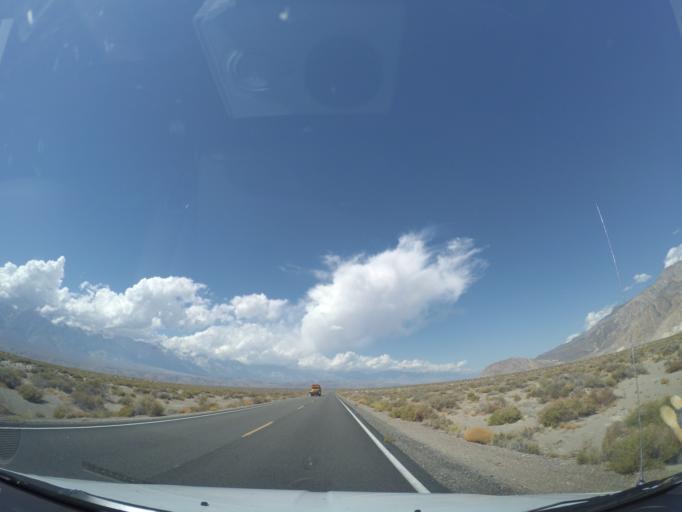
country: US
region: California
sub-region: Inyo County
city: Lone Pine
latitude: 36.5580
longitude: -117.9643
